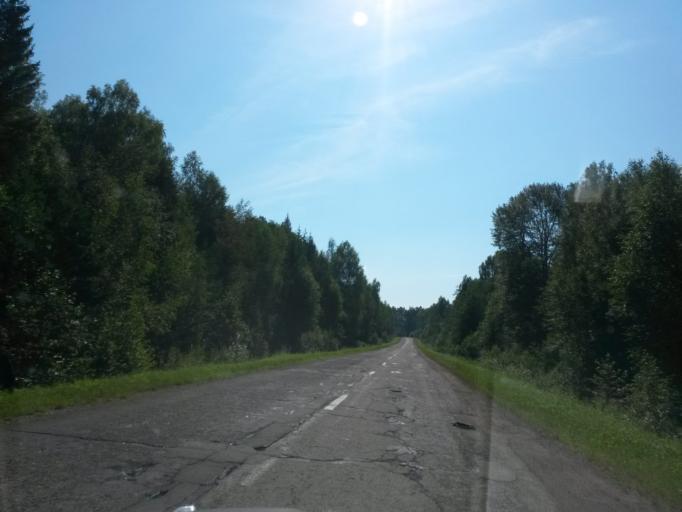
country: RU
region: Jaroslavl
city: Dubki
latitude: 57.2939
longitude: 40.0933
